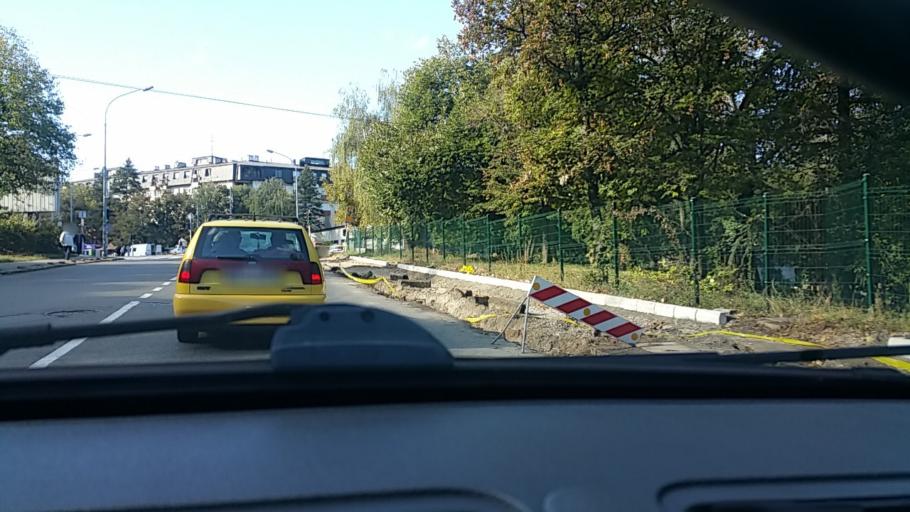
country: RS
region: Central Serbia
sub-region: Belgrade
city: Rakovica
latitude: 44.7535
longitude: 20.4557
